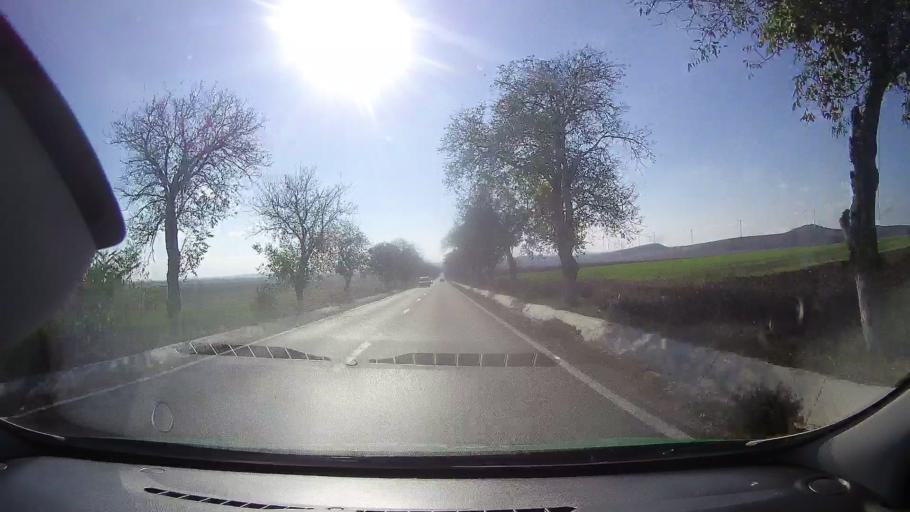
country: RO
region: Tulcea
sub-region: Comuna Ceamurlia de Jos
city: Ceamurlia de Jos
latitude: 44.8032
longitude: 28.6907
